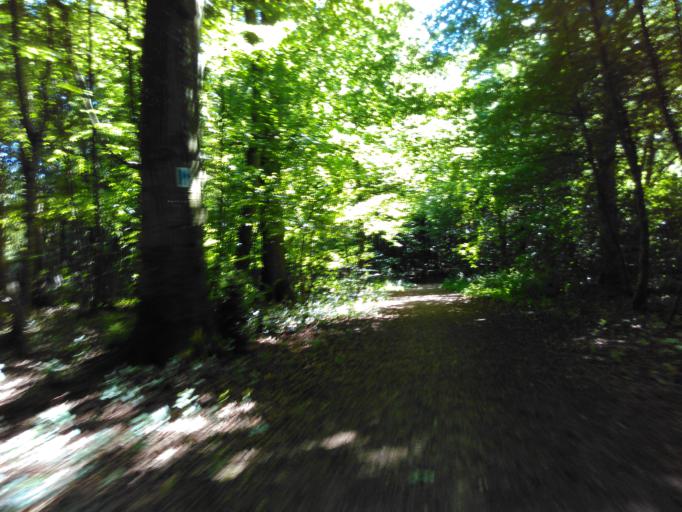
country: LU
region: Luxembourg
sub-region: Canton d'Esch-sur-Alzette
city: Leudelange
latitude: 49.5616
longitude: 6.0604
